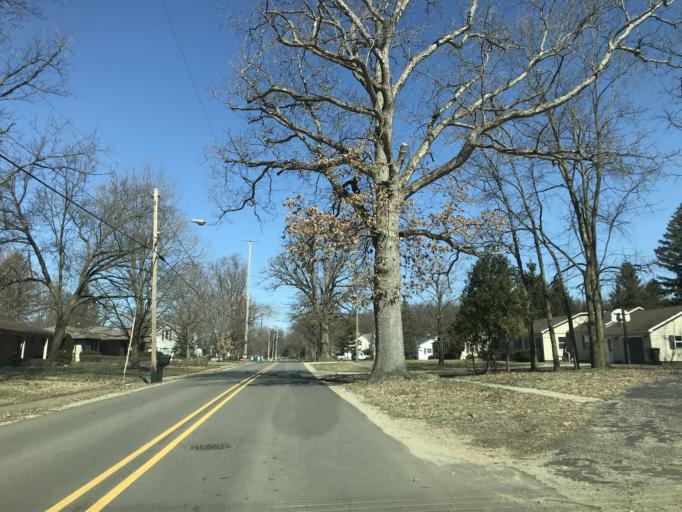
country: US
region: Michigan
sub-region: Hillsdale County
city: Jonesville
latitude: 41.9813
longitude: -84.6698
